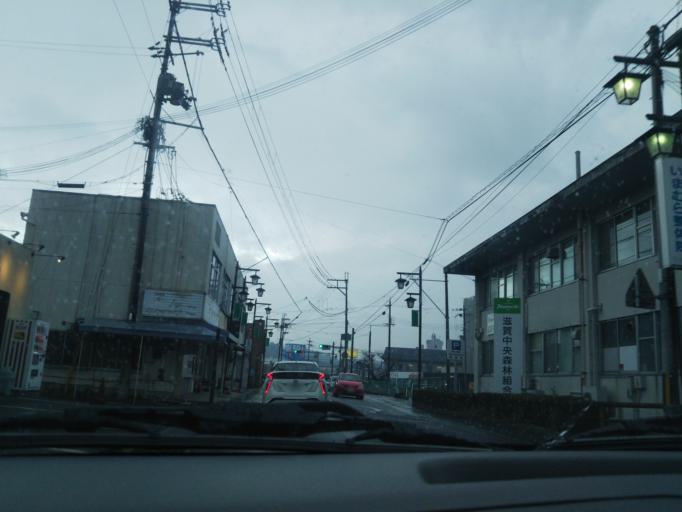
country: JP
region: Shiga Prefecture
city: Minakuchicho-matoba
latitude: 34.9680
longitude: 136.1726
